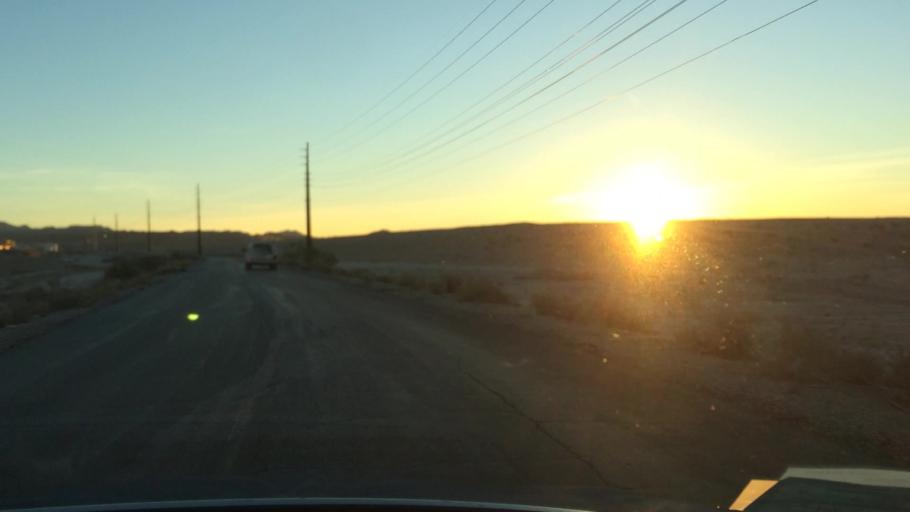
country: US
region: Nevada
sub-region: Clark County
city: Nellis Air Force Base
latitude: 36.2213
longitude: -114.8884
